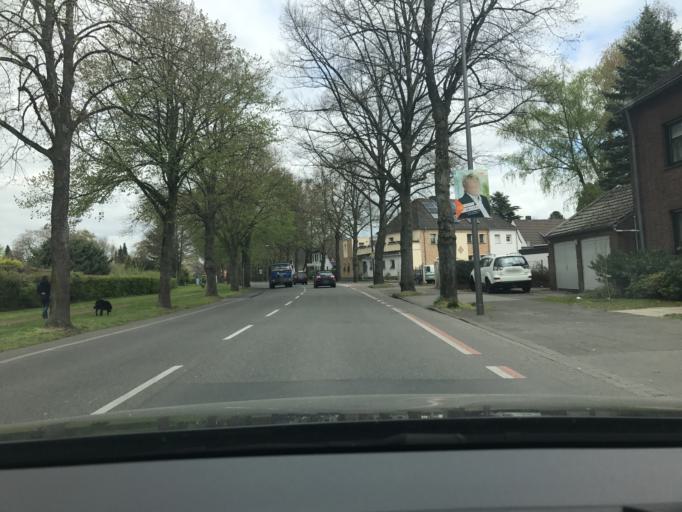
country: DE
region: North Rhine-Westphalia
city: Tonisvorst
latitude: 51.3171
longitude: 6.5352
